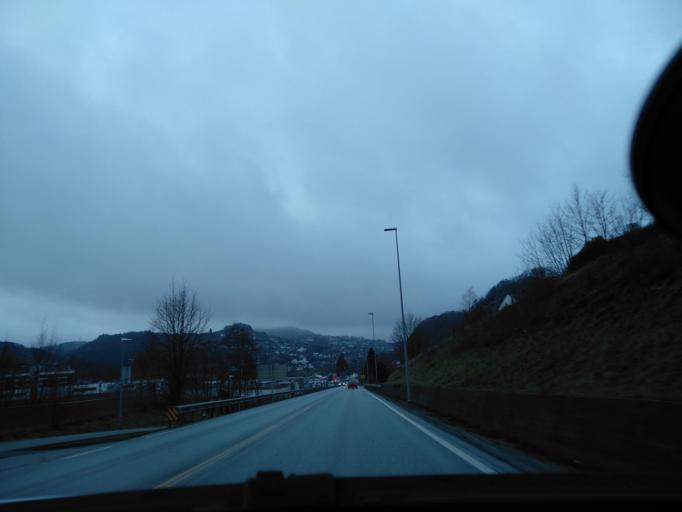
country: NO
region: Rogaland
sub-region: Gjesdal
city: Algard
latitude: 58.7701
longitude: 5.8540
